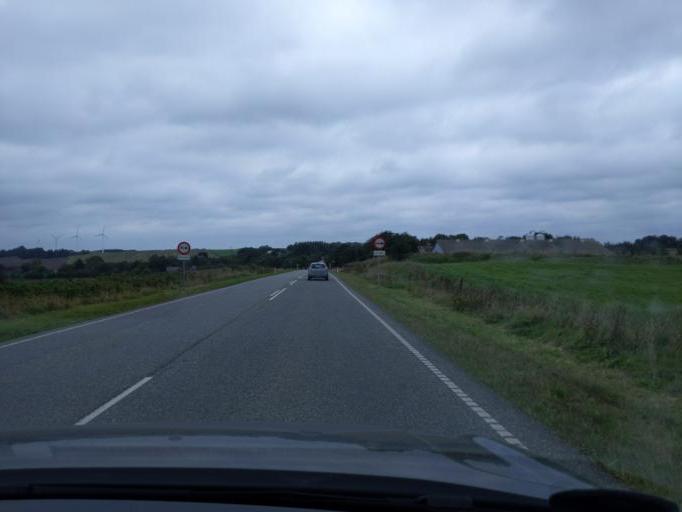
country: DK
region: North Denmark
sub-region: Mariagerfjord Kommune
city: Hobro
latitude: 56.5666
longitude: 9.8293
